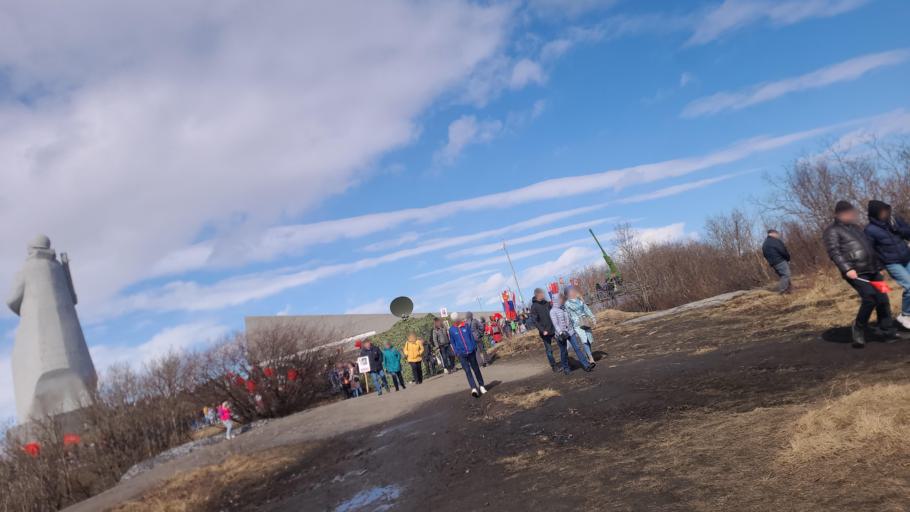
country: RU
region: Murmansk
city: Murmansk
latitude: 68.9920
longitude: 33.0734
